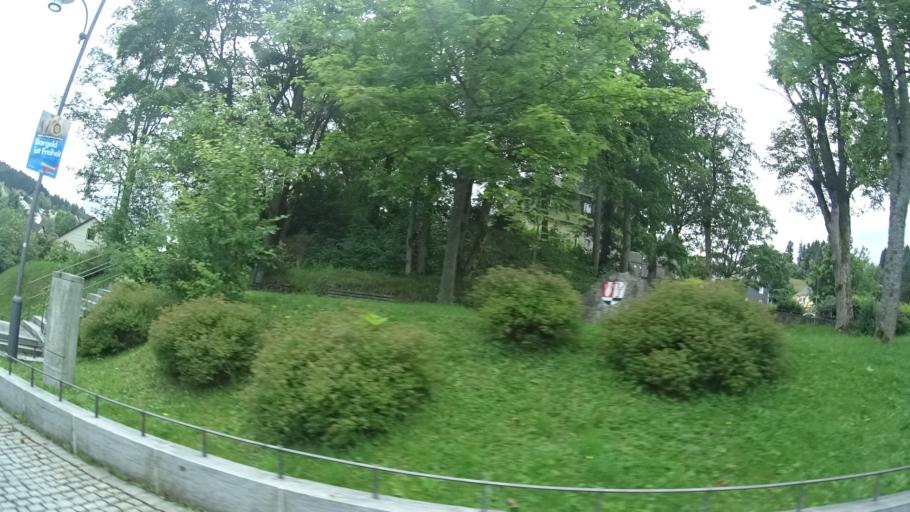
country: DE
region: Bavaria
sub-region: Upper Franconia
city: Tettau
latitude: 50.4689
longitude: 11.2587
